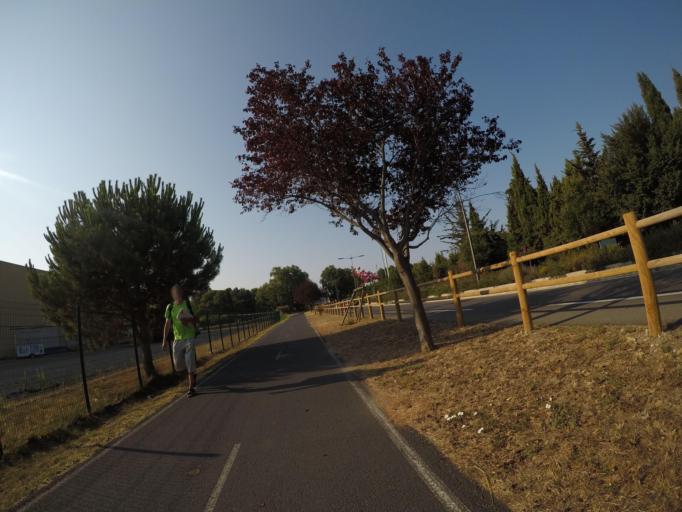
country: FR
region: Languedoc-Roussillon
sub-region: Departement des Pyrenees-Orientales
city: Canohes
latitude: 42.6601
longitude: 2.8344
